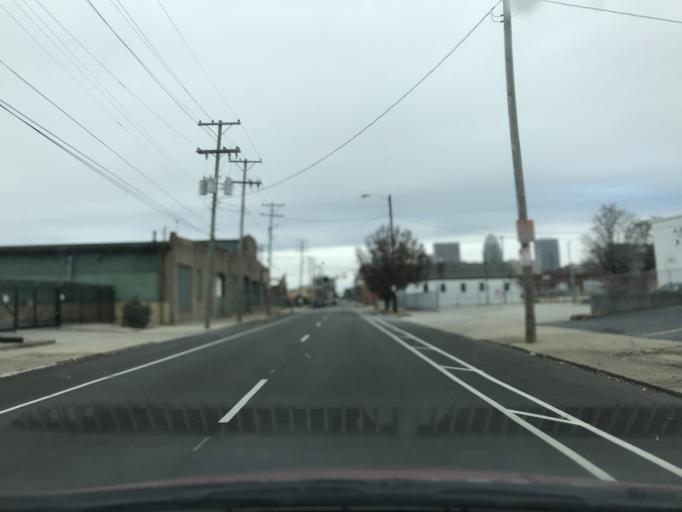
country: US
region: Kentucky
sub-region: Jefferson County
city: Louisville
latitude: 38.2418
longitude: -85.7642
